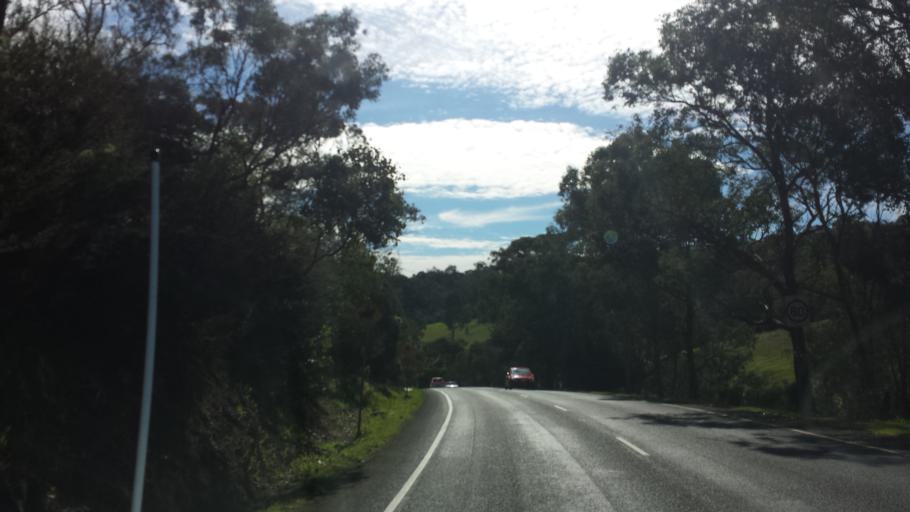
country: AU
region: Victoria
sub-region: Nillumbik
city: Wattleglen
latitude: -37.6772
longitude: 145.2063
